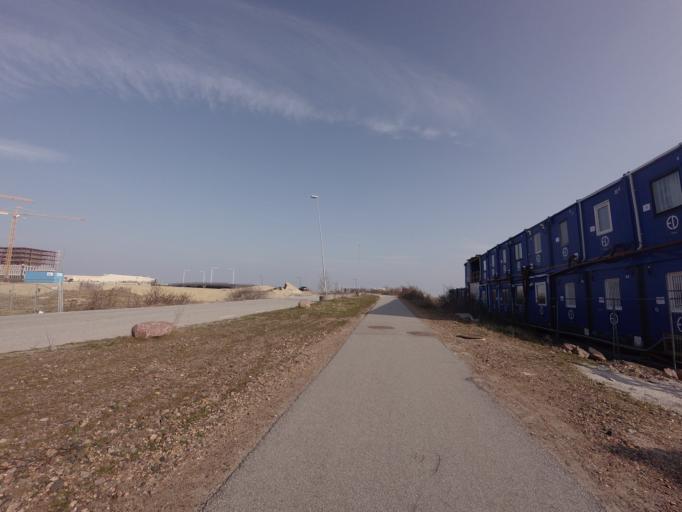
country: SE
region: Skane
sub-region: Malmo
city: Bunkeflostrand
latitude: 55.5640
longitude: 12.9830
